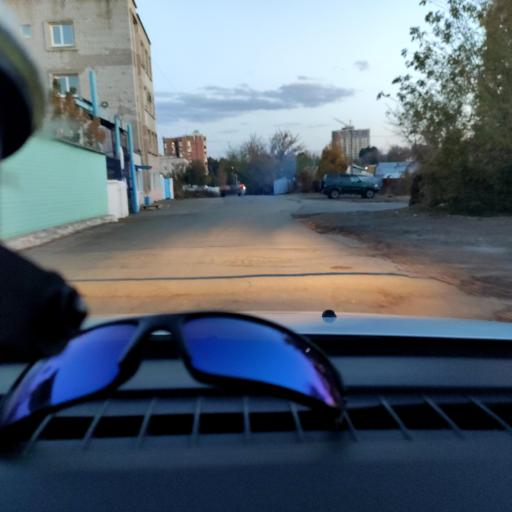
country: RU
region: Samara
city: Samara
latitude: 53.2255
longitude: 50.2253
